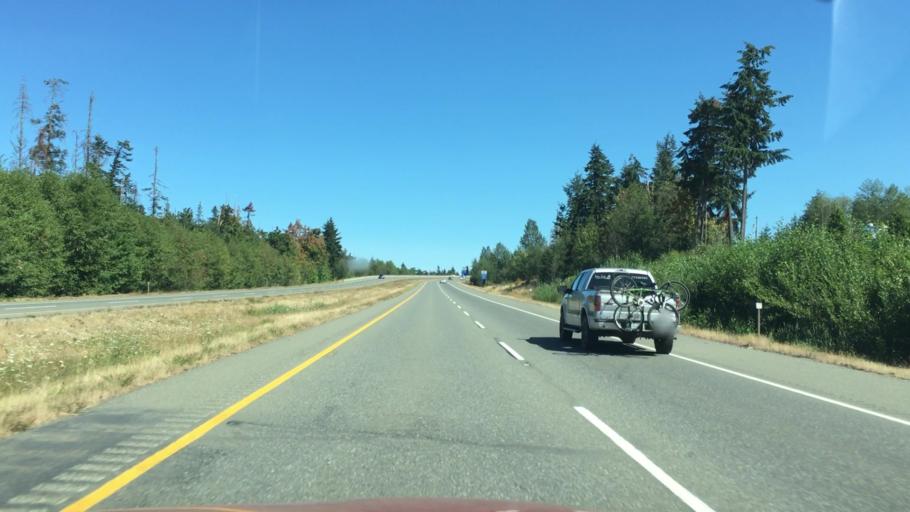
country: CA
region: British Columbia
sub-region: Regional District of Nanaimo
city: Parksville
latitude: 49.3136
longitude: -124.3533
